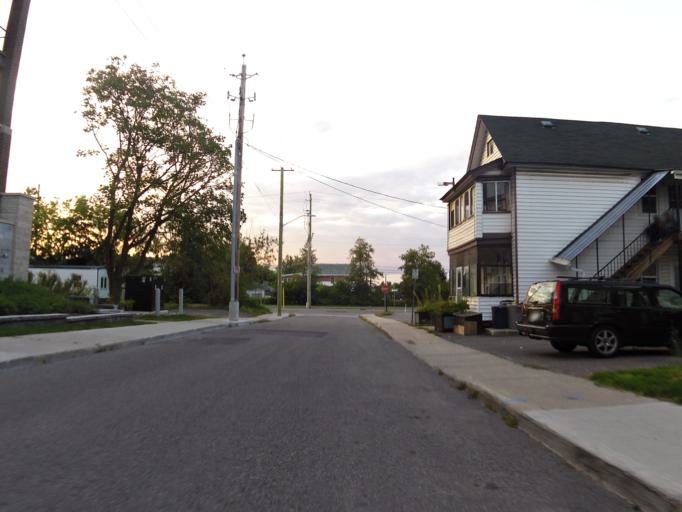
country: CA
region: Ontario
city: Ottawa
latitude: 45.4059
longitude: -75.7280
